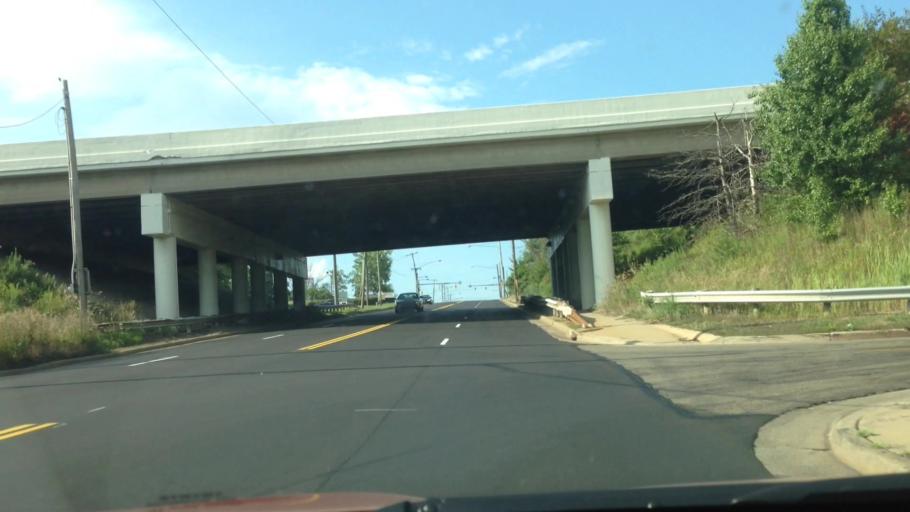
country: US
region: Ohio
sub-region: Summit County
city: Portage Lakes
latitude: 41.0255
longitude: -81.4915
